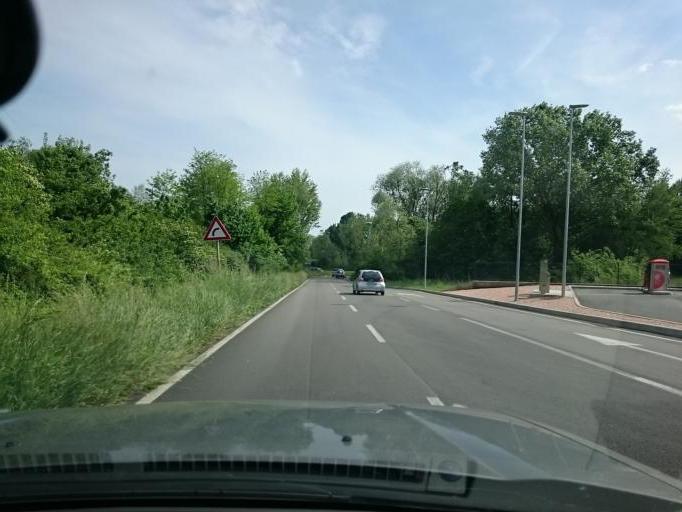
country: IT
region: Veneto
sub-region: Provincia di Padova
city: Noventa
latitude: 45.4090
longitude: 11.9189
